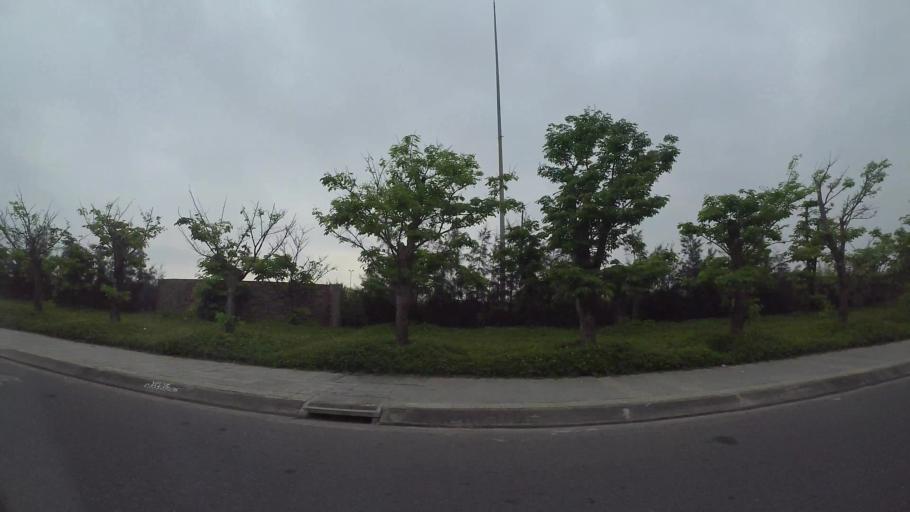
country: VN
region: Da Nang
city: Son Tra
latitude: 16.0785
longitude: 108.2459
